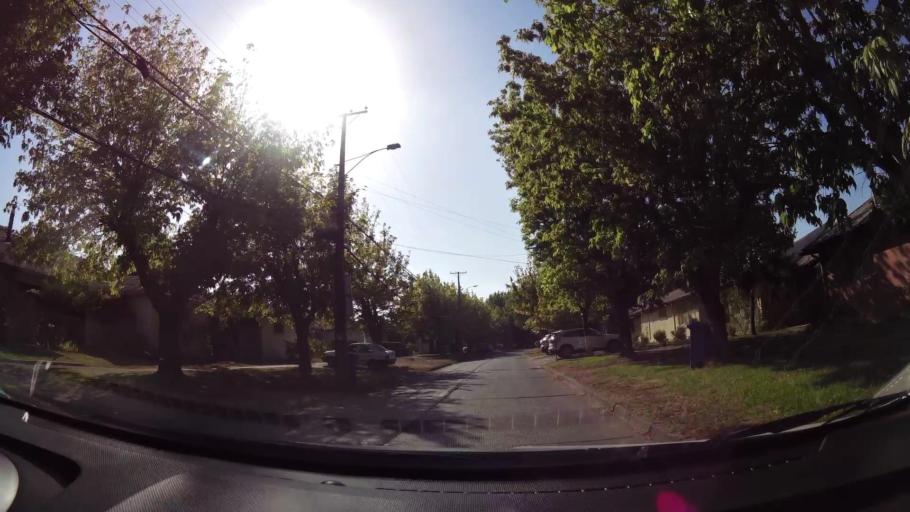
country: CL
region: Maule
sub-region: Provincia de Talca
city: Talca
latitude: -35.4172
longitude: -71.6668
